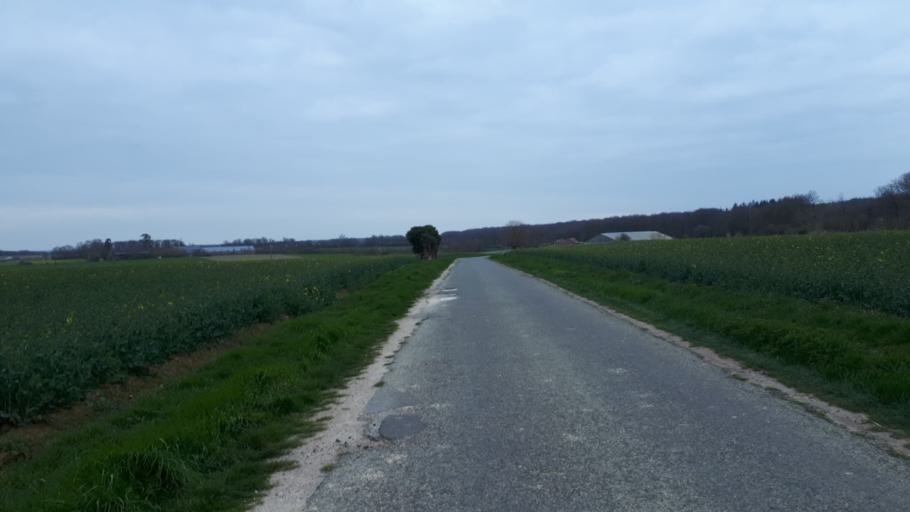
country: FR
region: Centre
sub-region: Departement du Loir-et-Cher
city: Aze
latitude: 47.8350
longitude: 1.0120
